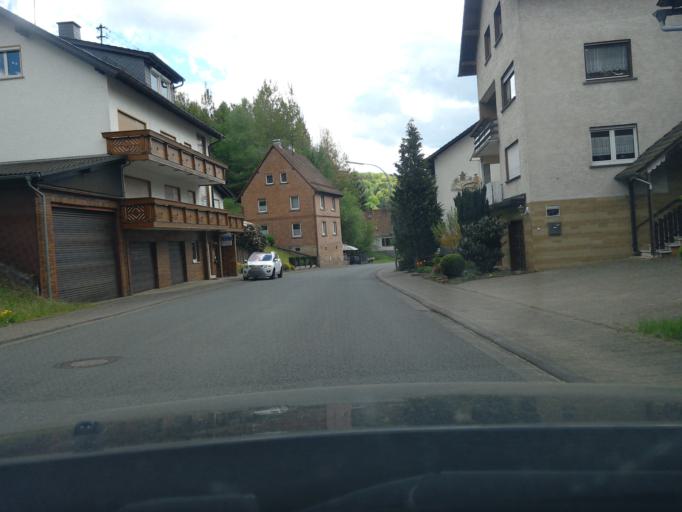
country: DE
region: Bavaria
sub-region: Regierungsbezirk Unterfranken
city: Frammersbach
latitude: 50.1293
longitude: 9.4765
